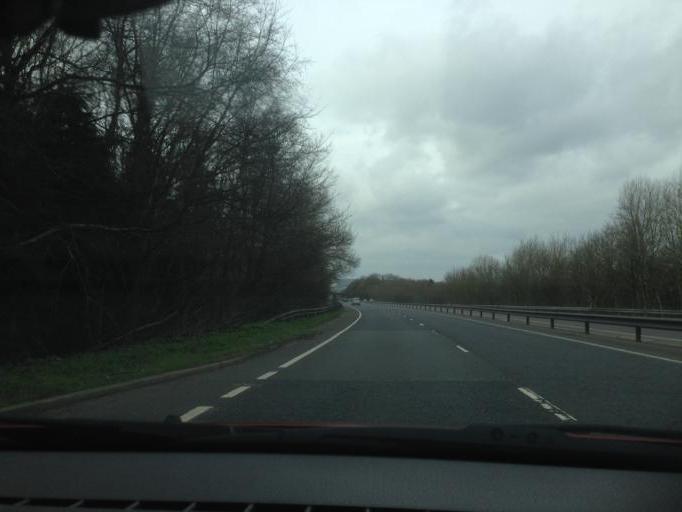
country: GB
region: England
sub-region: Kent
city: Sevenoaks
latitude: 51.2662
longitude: 0.1690
